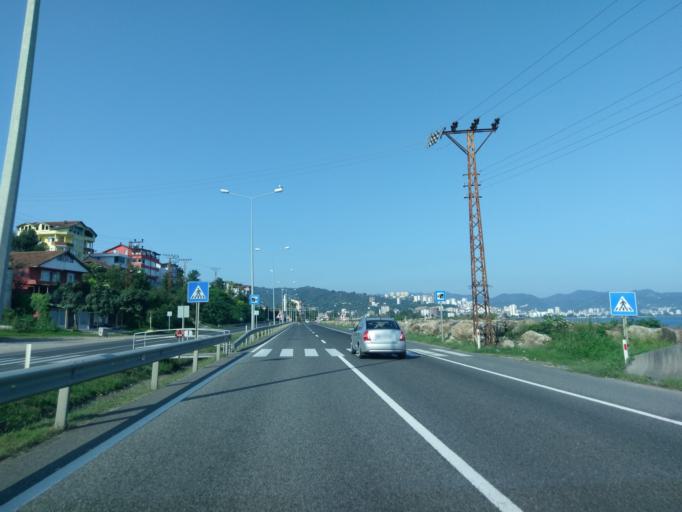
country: TR
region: Ordu
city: Fatsa
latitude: 41.0219
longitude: 37.5437
